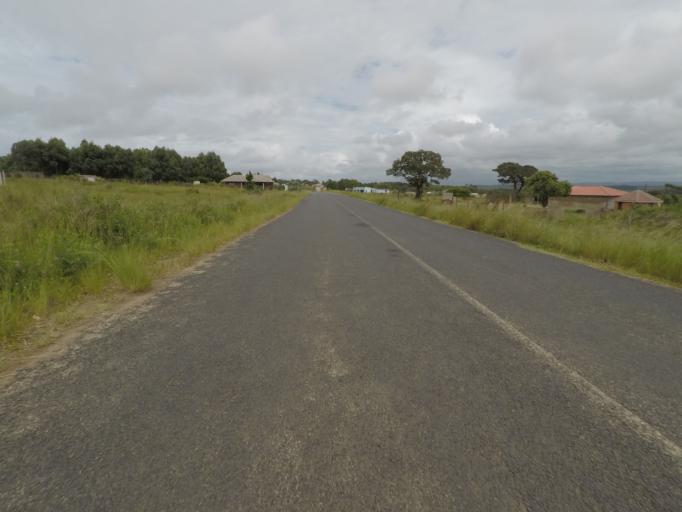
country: ZA
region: KwaZulu-Natal
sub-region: uThungulu District Municipality
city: eSikhawini
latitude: -28.9134
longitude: 31.8528
